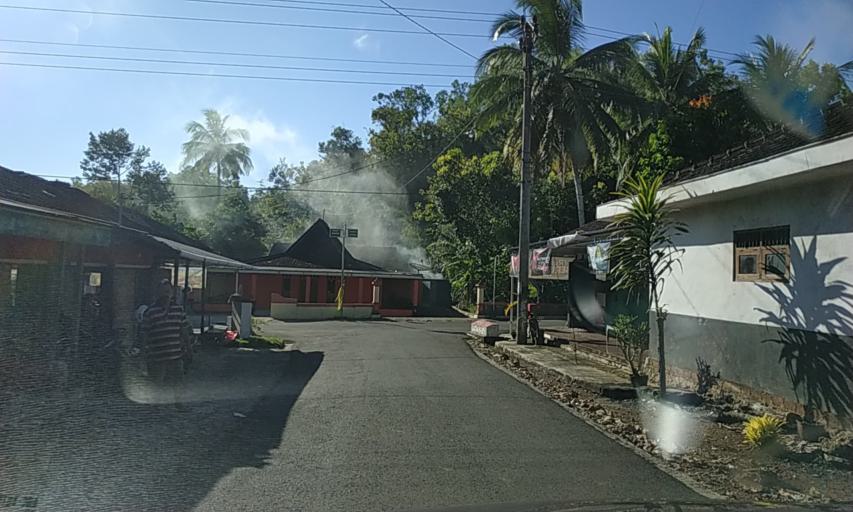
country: ID
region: East Java
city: Krajan
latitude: -8.1139
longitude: 110.8706
